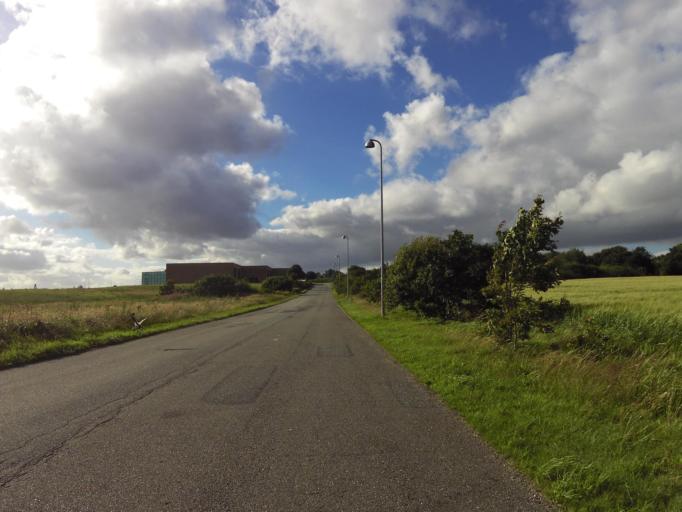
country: DK
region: South Denmark
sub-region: Tonder Kommune
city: Toftlund
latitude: 55.1782
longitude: 9.0683
